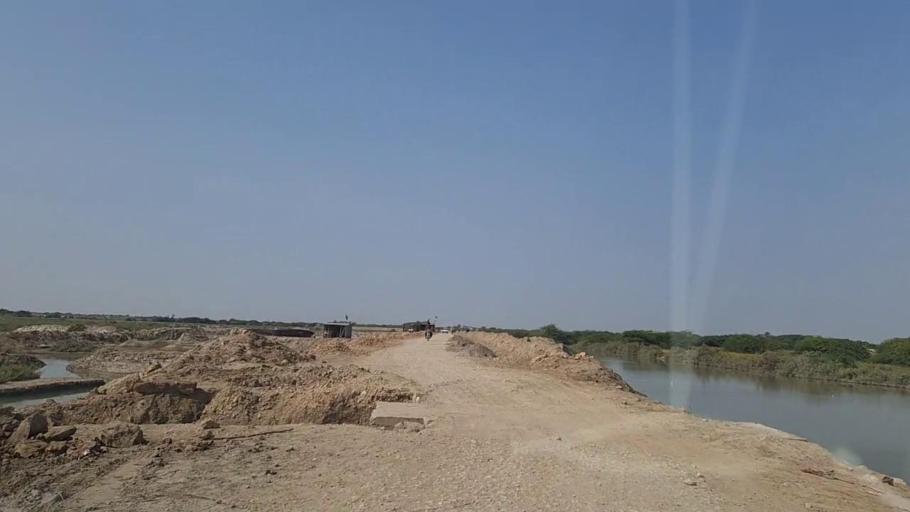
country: PK
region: Sindh
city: Chuhar Jamali
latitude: 24.1949
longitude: 67.8387
